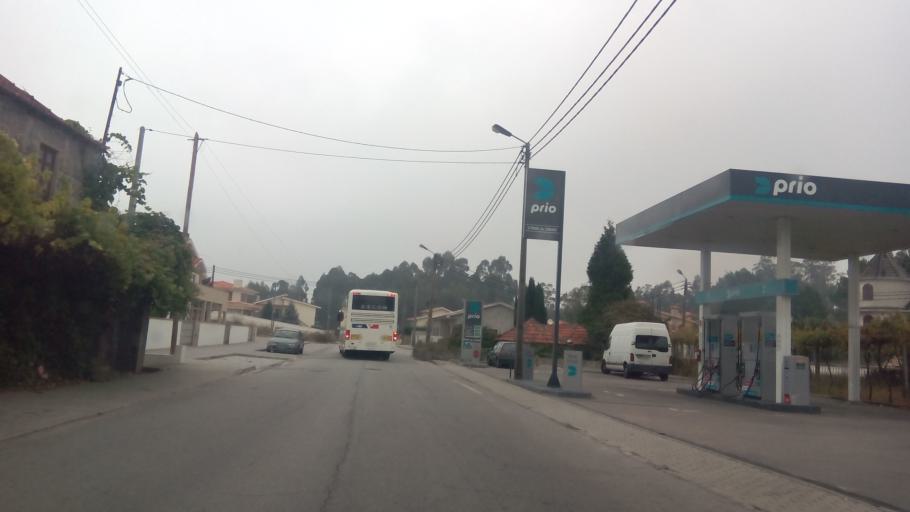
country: PT
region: Porto
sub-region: Paredes
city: Rebordosa
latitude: 41.2162
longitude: -8.3802
